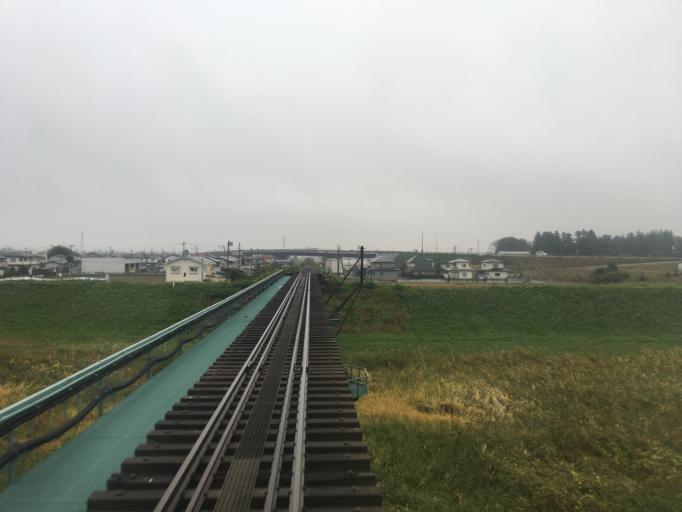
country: JP
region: Miyagi
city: Furukawa
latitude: 38.5693
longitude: 140.9806
